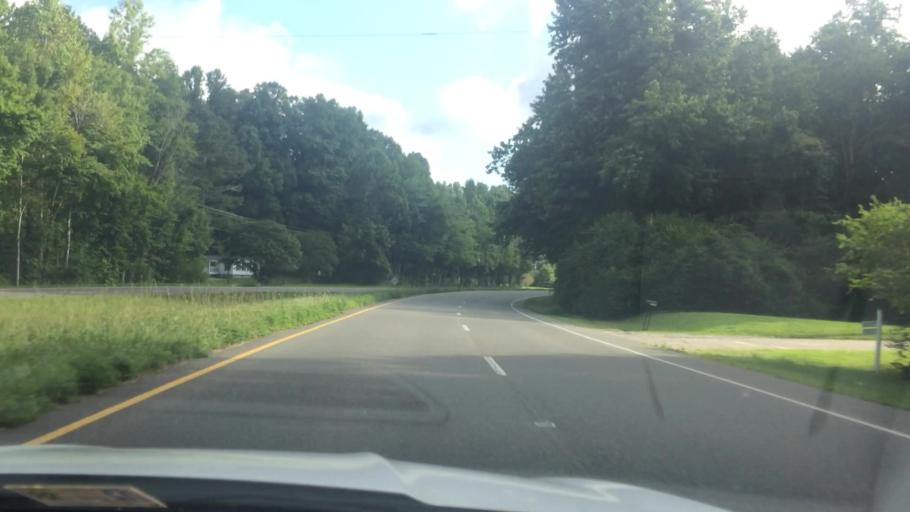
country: US
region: Virginia
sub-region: Gloucester County
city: Gloucester Courthouse
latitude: 37.4511
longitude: -76.4716
